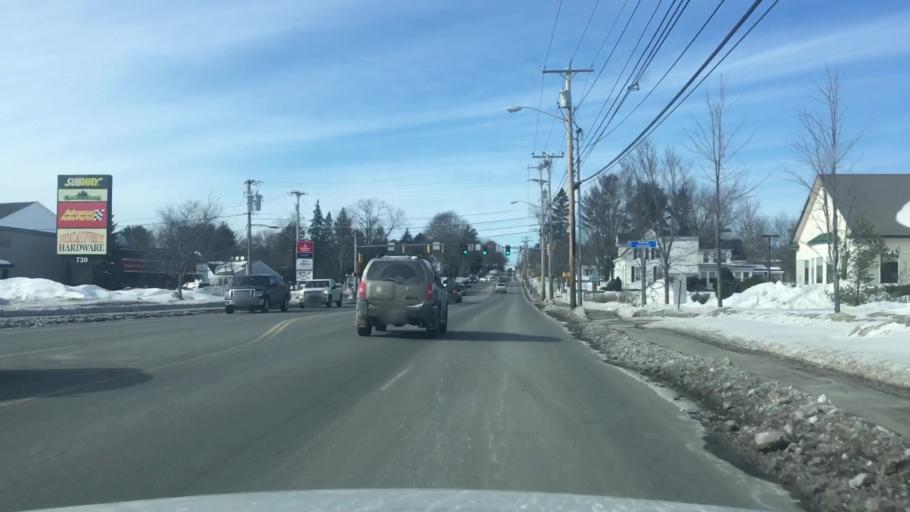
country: US
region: Maine
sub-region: Penobscot County
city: Bangor
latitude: 44.8249
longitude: -68.7807
